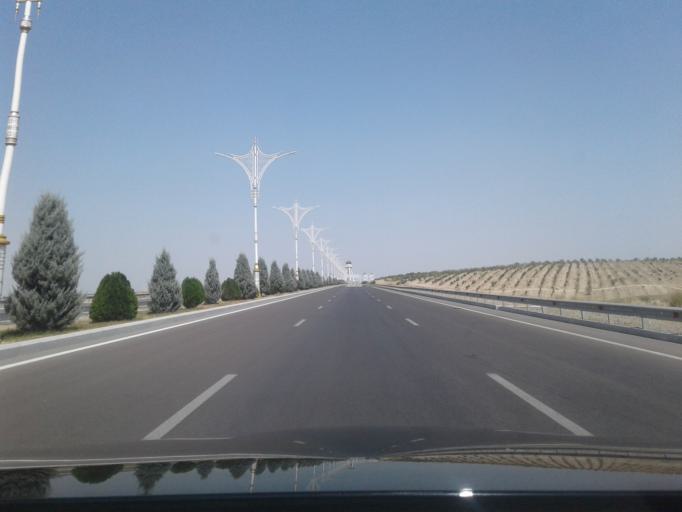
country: TM
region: Ahal
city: Ashgabat
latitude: 37.8783
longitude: 58.4113
